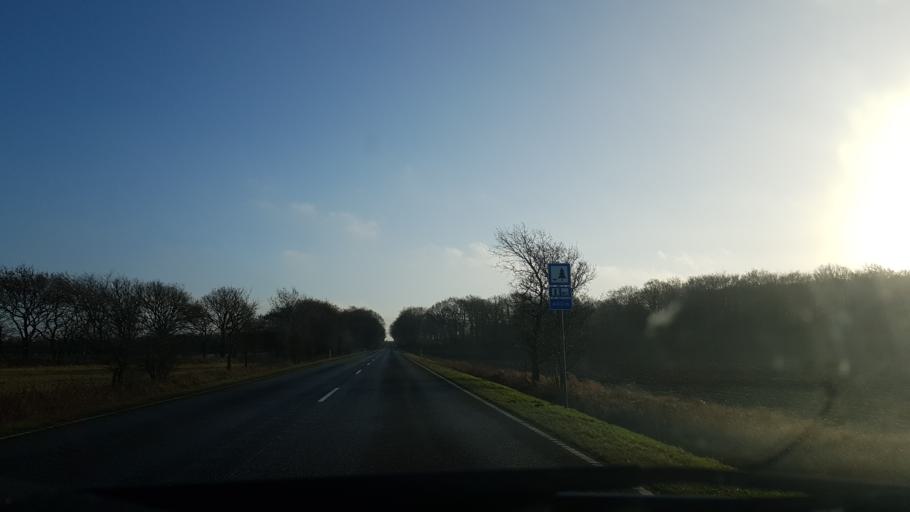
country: DK
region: South Denmark
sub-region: Tonder Kommune
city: Toftlund
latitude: 55.2249
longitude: 9.1749
